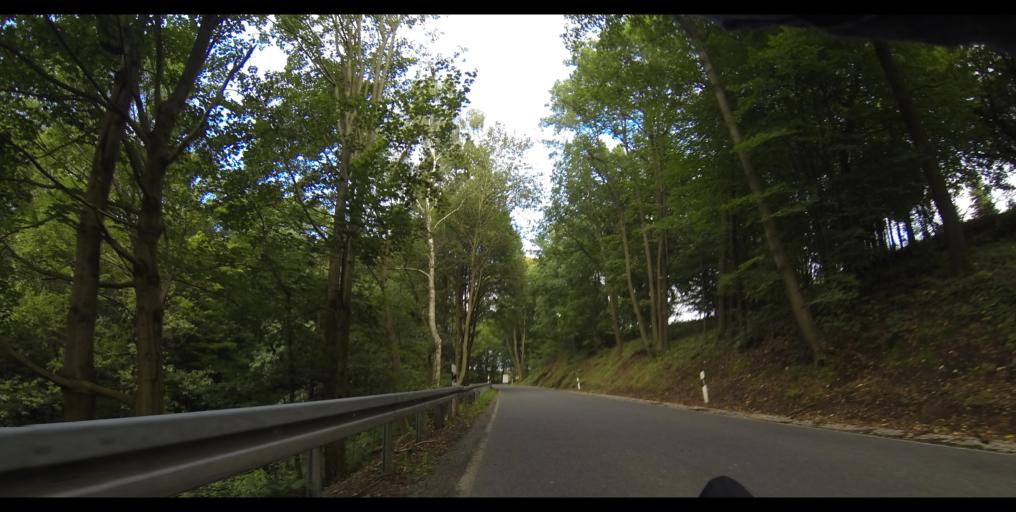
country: DE
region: Saxony
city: Hainichen
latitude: 50.9846
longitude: 13.1443
